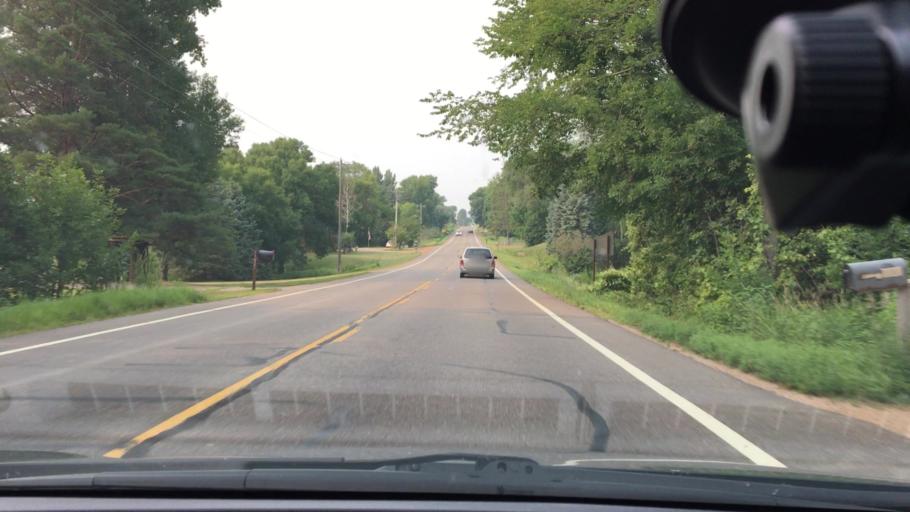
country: US
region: Minnesota
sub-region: Hennepin County
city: Champlin
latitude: 45.1688
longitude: -93.4621
